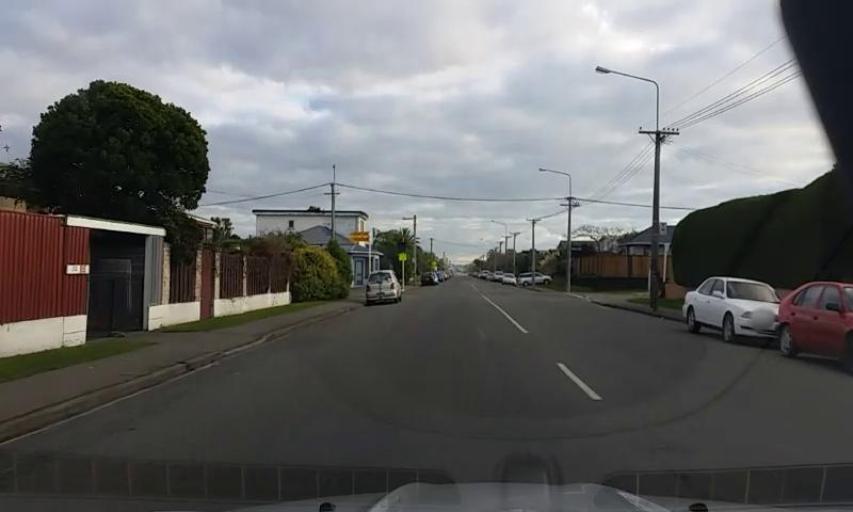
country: NZ
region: Canterbury
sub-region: Christchurch City
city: Christchurch
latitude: -43.5282
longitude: 172.7348
